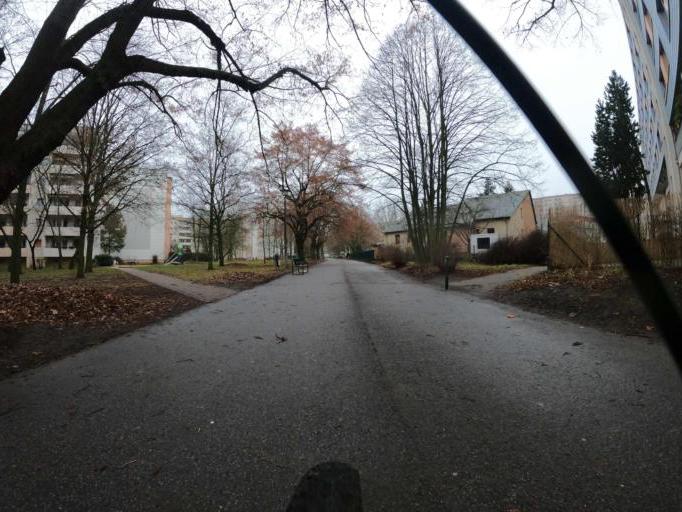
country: DE
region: Berlin
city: Marzahn
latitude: 52.5588
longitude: 13.5652
